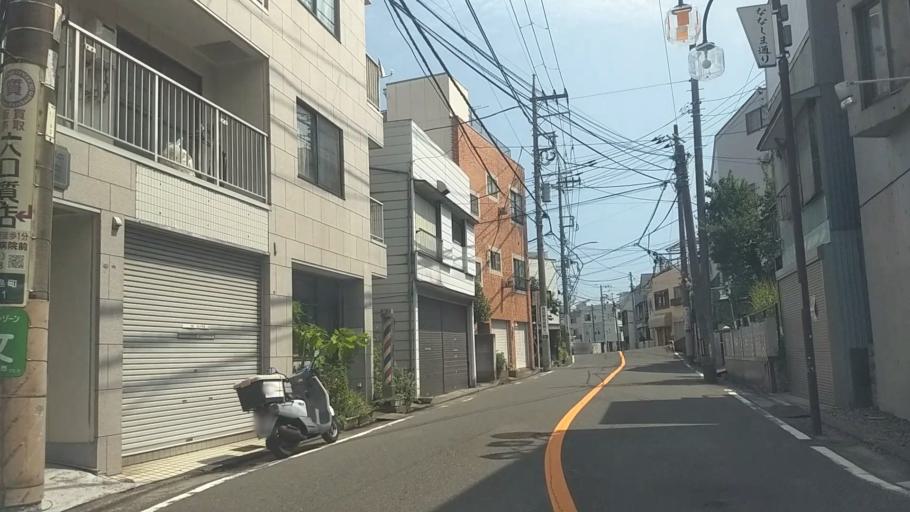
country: JP
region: Kanagawa
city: Yokohama
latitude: 35.4886
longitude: 139.6435
